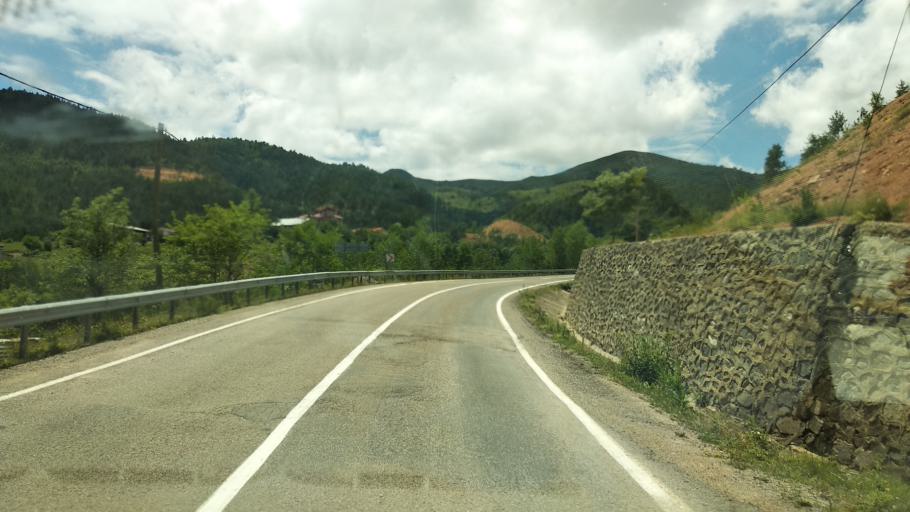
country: TR
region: Gumushane
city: Kose
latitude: 40.3044
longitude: 39.5570
